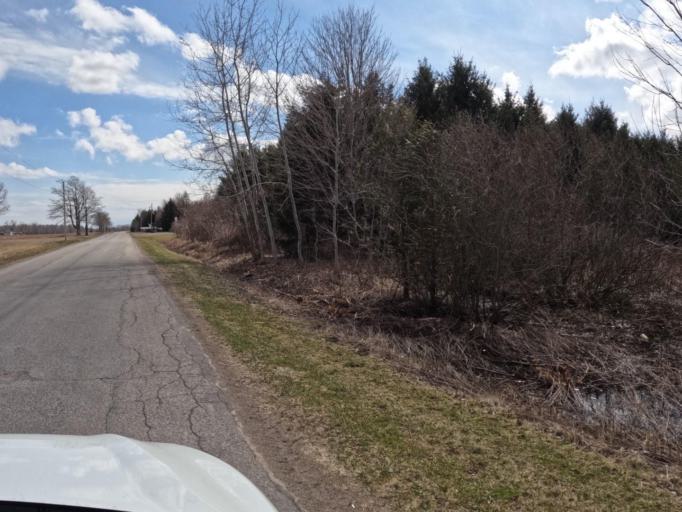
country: CA
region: Ontario
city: Norfolk County
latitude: 42.9069
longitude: -80.1922
